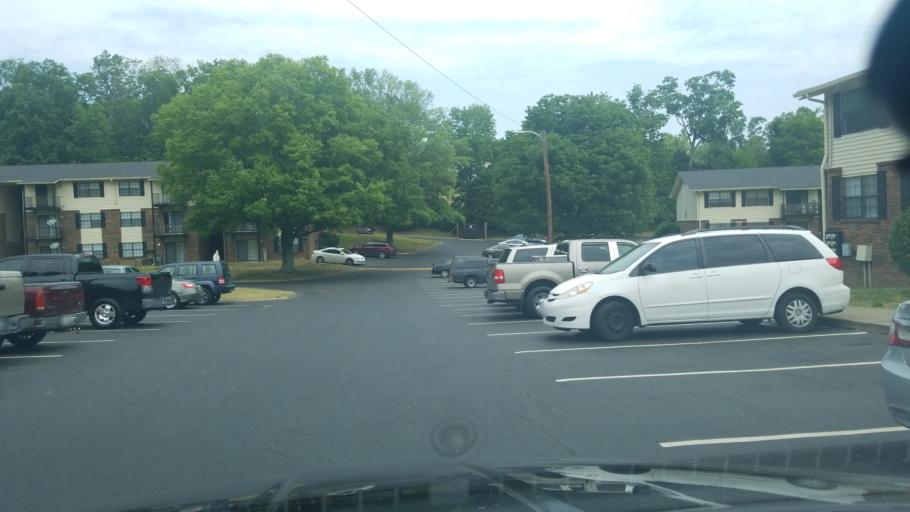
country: US
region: Tennessee
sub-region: Davidson County
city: Goodlettsville
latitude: 36.2526
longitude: -86.7409
